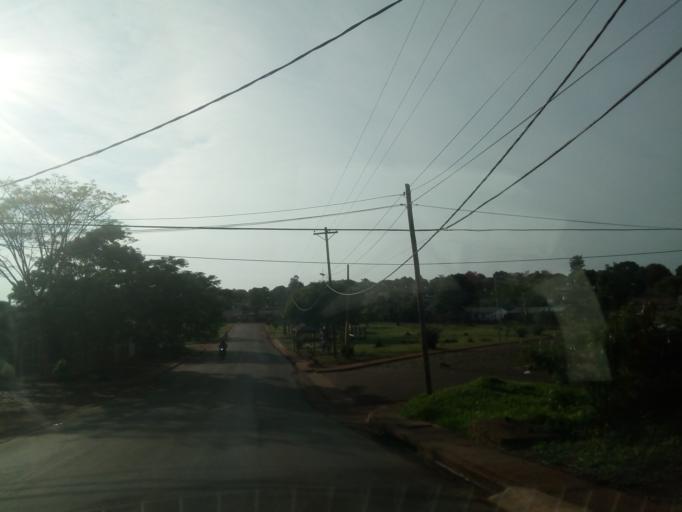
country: AR
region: Misiones
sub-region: Departamento de Capital
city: Posadas
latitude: -27.4311
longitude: -55.9107
